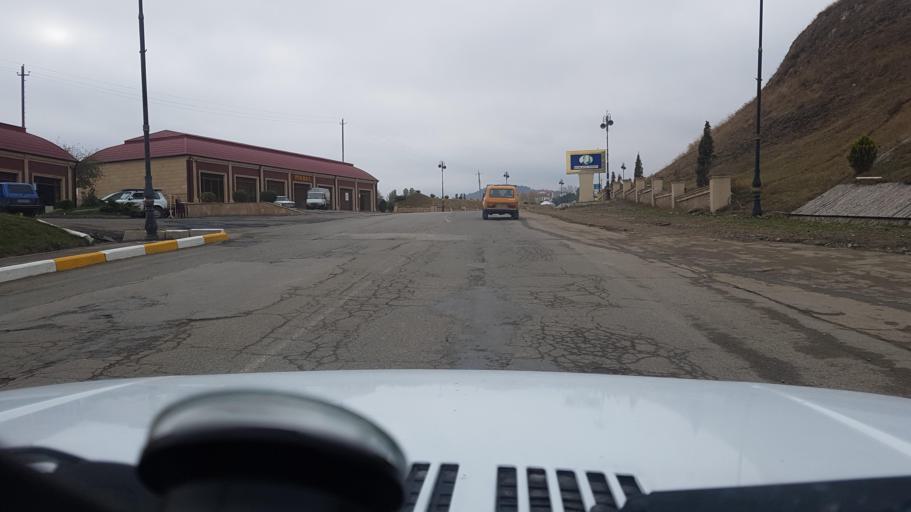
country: AZ
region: Gadabay Rayon
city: Ariqdam
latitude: 40.5849
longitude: 45.8109
